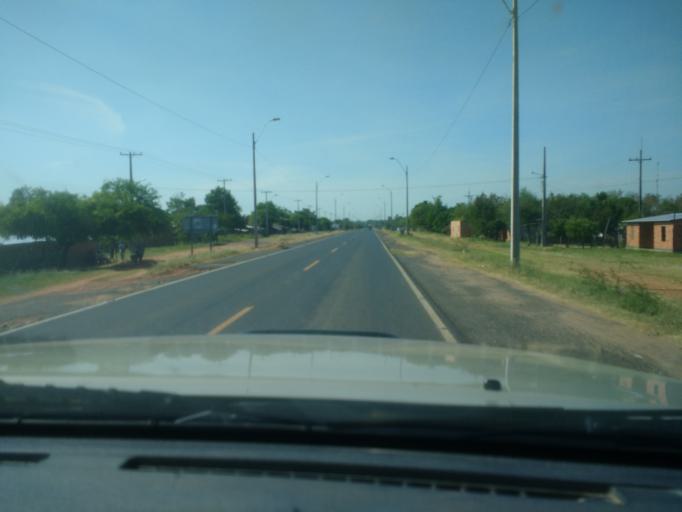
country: PY
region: Presidente Hayes
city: Benjamin Aceval
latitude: -24.9468
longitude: -57.5524
